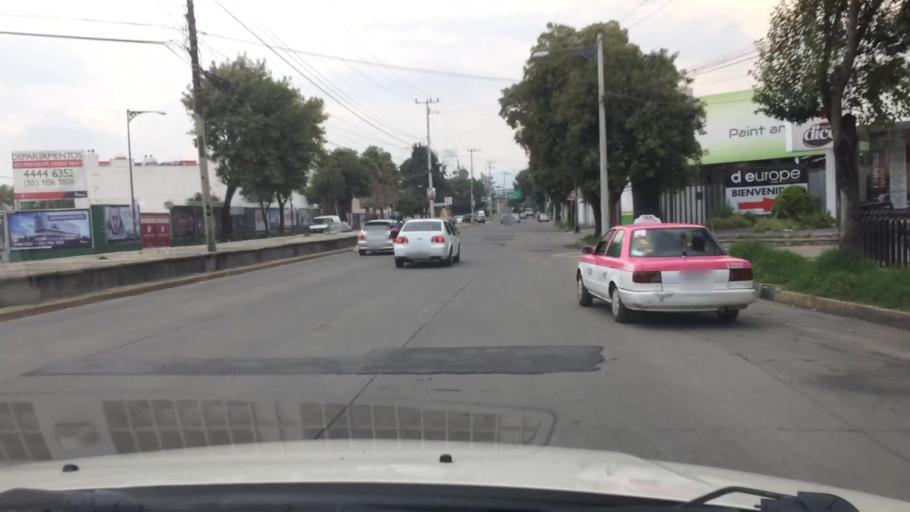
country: MX
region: Mexico City
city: Coyoacan
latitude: 19.3250
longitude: -99.1398
